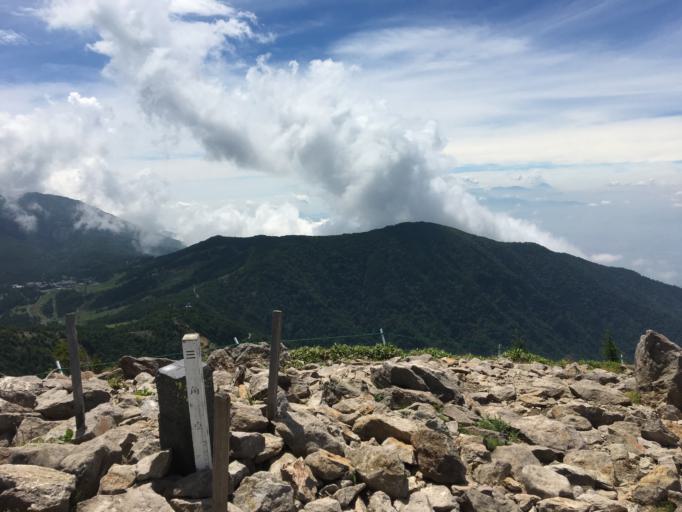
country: JP
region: Nagano
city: Komoro
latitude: 36.4193
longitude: 138.4471
